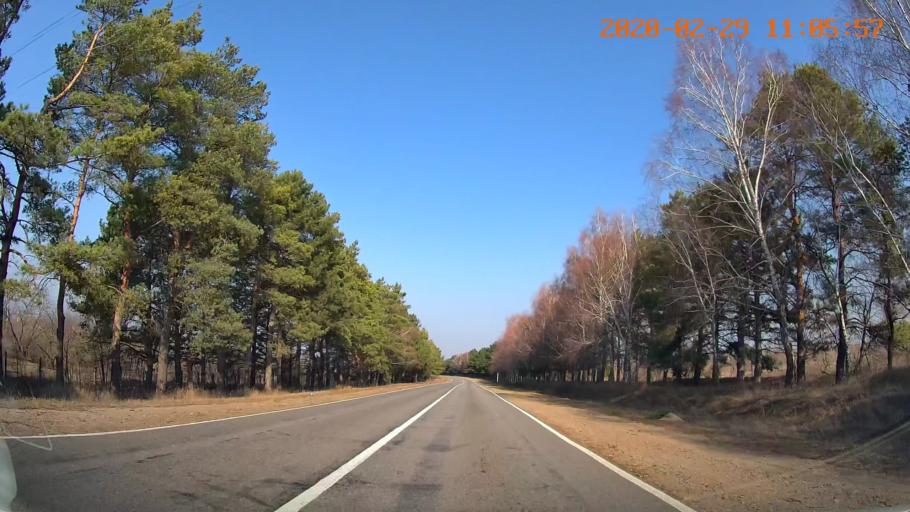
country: MD
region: Criuleni
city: Criuleni
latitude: 47.2085
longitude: 29.1899
